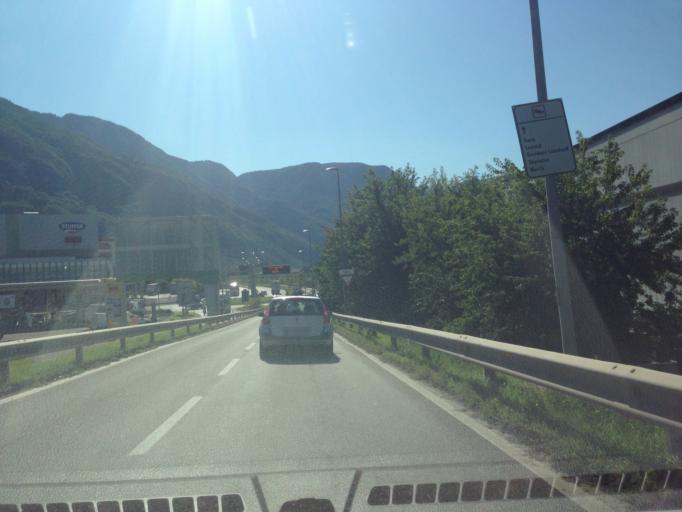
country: IT
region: Trentino-Alto Adige
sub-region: Bolzano
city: San Giacomo
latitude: 46.4721
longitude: 11.3155
